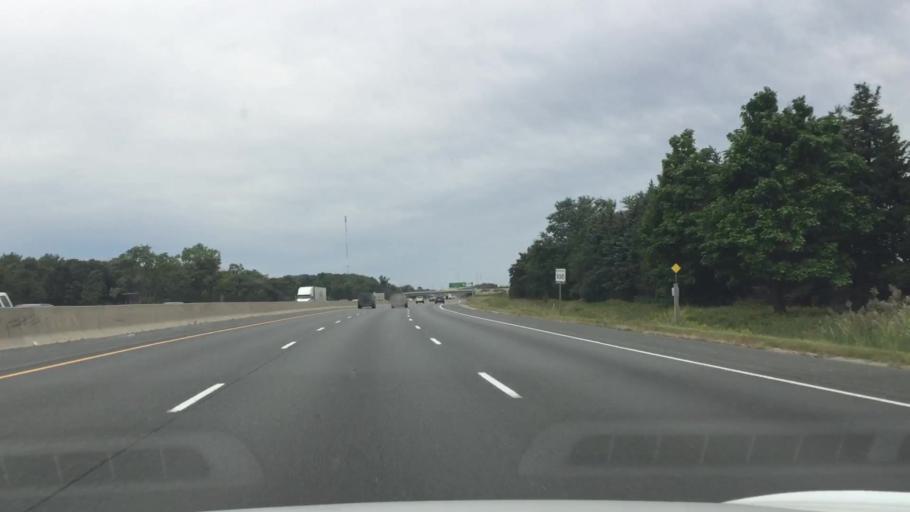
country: CA
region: Ontario
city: Dorchester
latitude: 42.9444
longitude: -81.1143
